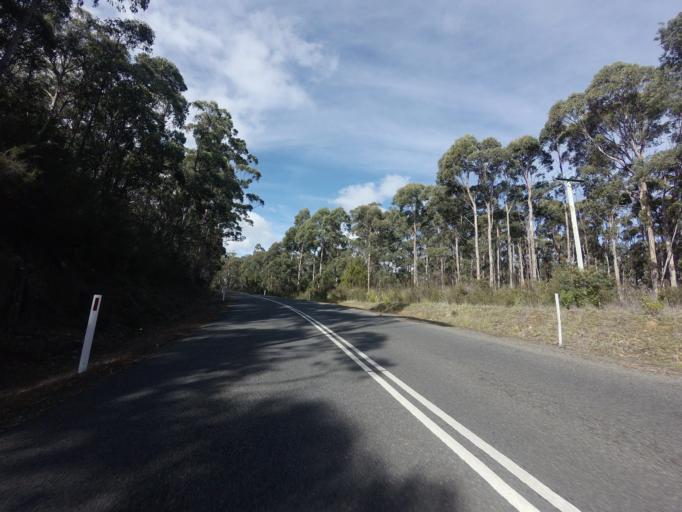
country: AU
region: Tasmania
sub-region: Clarence
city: Sandford
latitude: -43.1303
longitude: 147.7826
